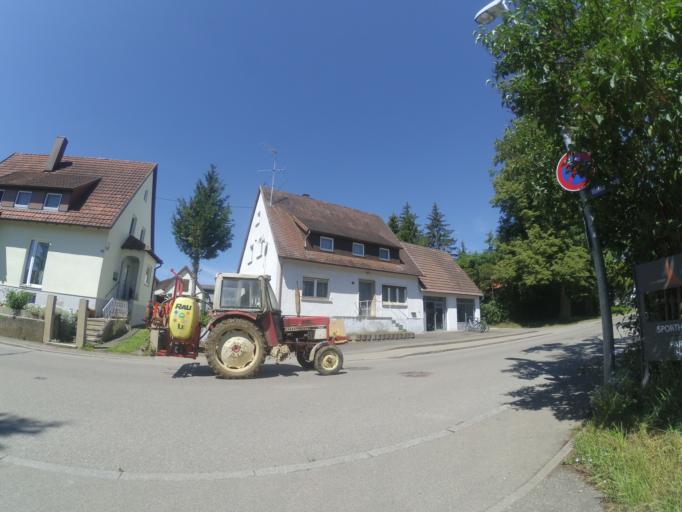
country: DE
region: Baden-Wuerttemberg
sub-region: Tuebingen Region
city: Dornstadt
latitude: 48.4796
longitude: 9.9068
